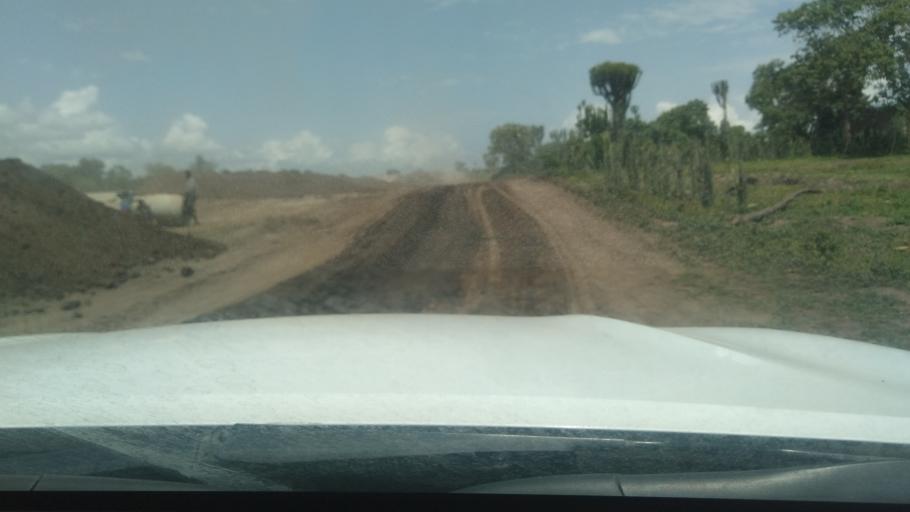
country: ET
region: Oromiya
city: Shashemene
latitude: 7.2792
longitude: 38.6043
